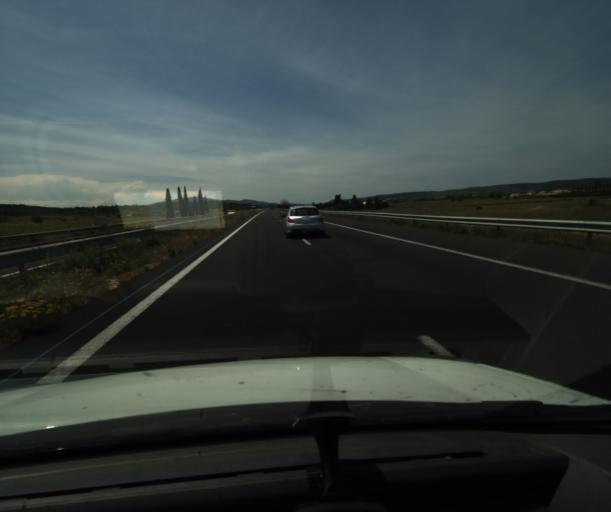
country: FR
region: Languedoc-Roussillon
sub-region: Departement de l'Aude
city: Lezignan-Corbieres
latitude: 43.1703
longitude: 2.7857
